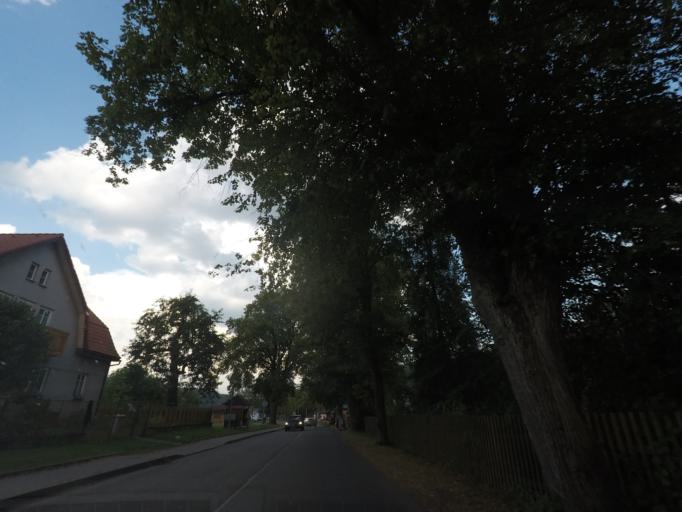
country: CZ
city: Teplice nad Metuji
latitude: 50.6173
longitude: 16.1209
